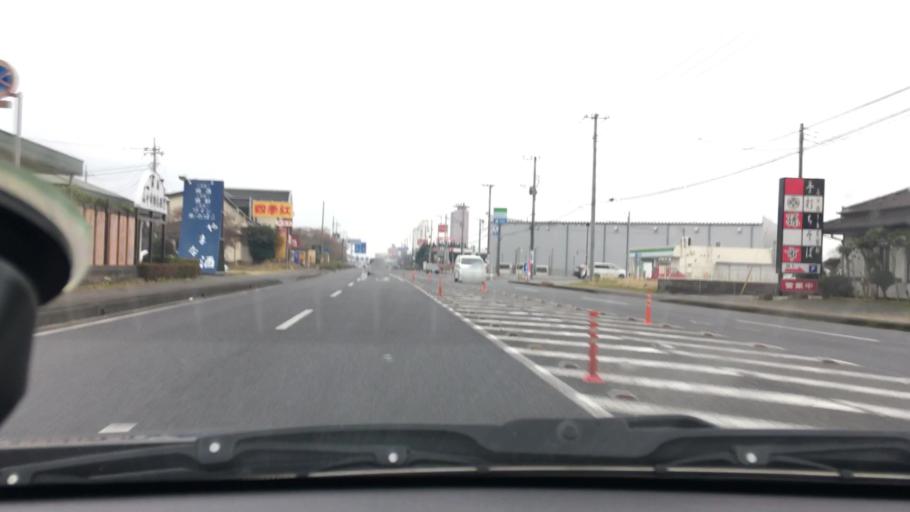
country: JP
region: Chiba
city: Omigawa
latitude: 35.9043
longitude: 140.6285
